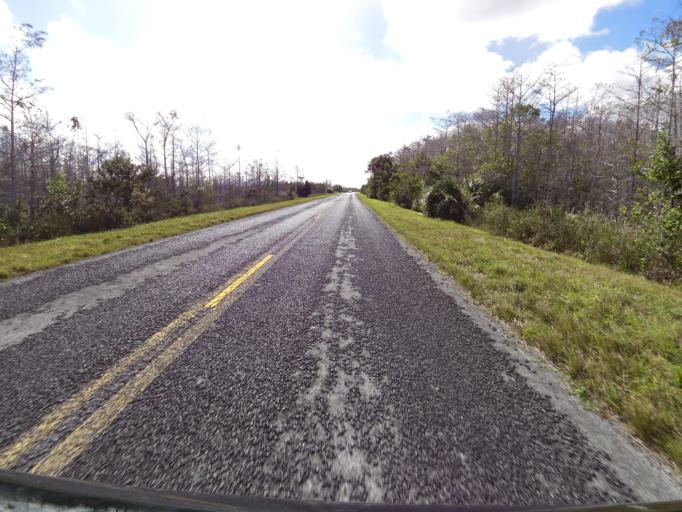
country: US
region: Florida
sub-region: Miami-Dade County
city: Florida City
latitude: 25.4070
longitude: -80.7870
